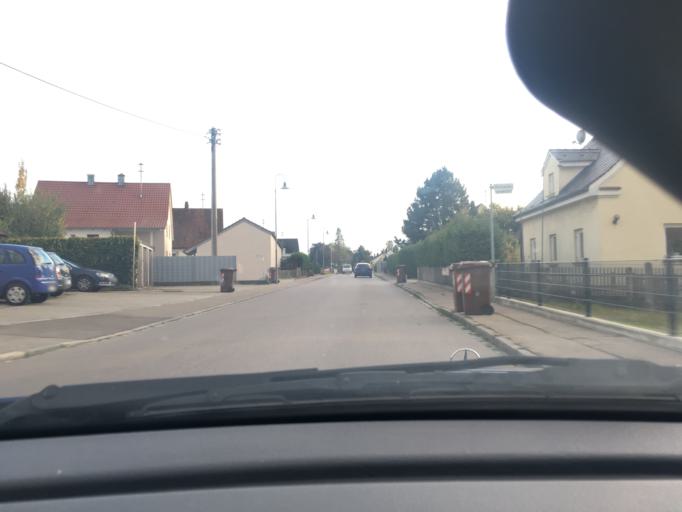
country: DE
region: Bavaria
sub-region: Swabia
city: Gablingen
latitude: 48.4088
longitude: 10.8235
